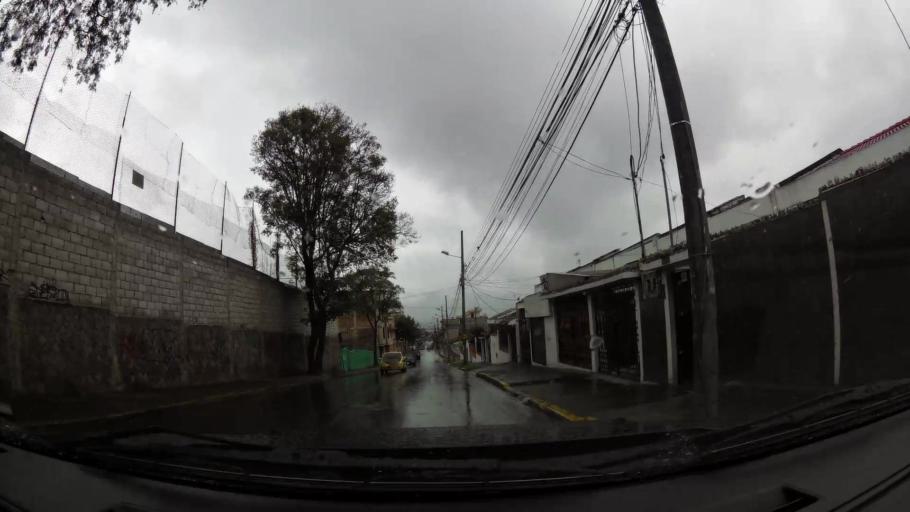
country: EC
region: Pichincha
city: Quito
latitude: -0.1191
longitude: -78.4970
